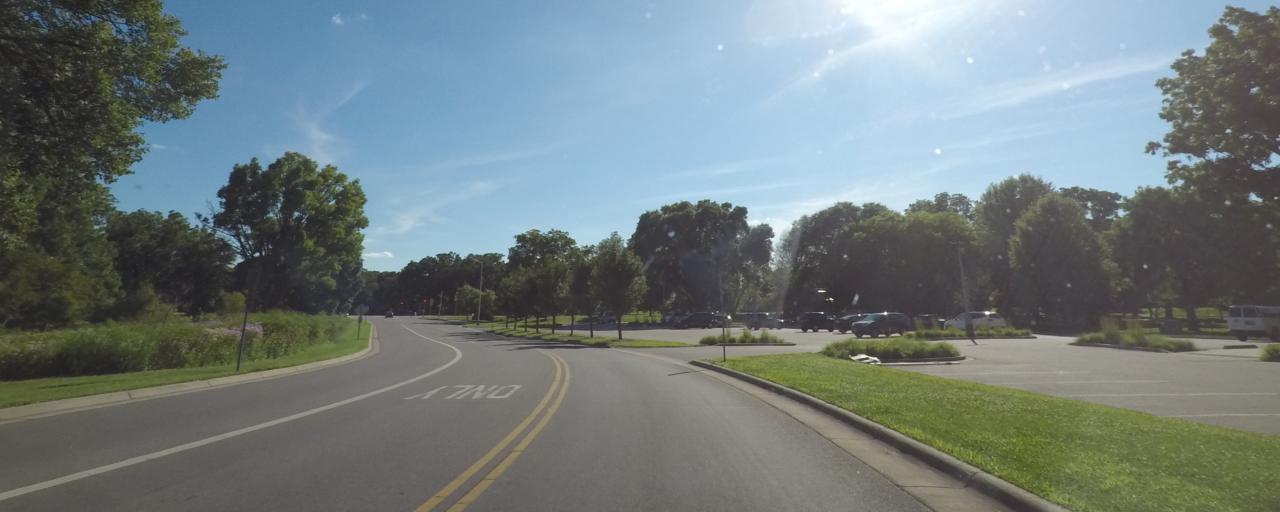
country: US
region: Wisconsin
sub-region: Rock County
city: Janesville
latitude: 42.6765
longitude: -88.9913
